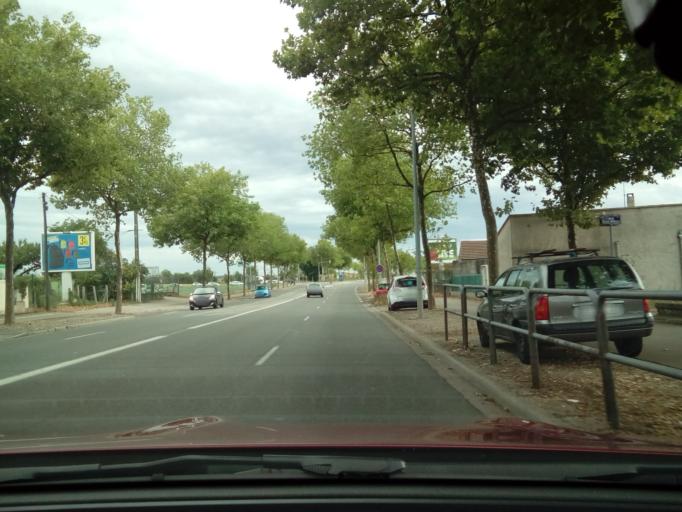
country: FR
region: Rhone-Alpes
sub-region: Departement du Rhone
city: Bron
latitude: 45.7469
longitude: 4.9365
